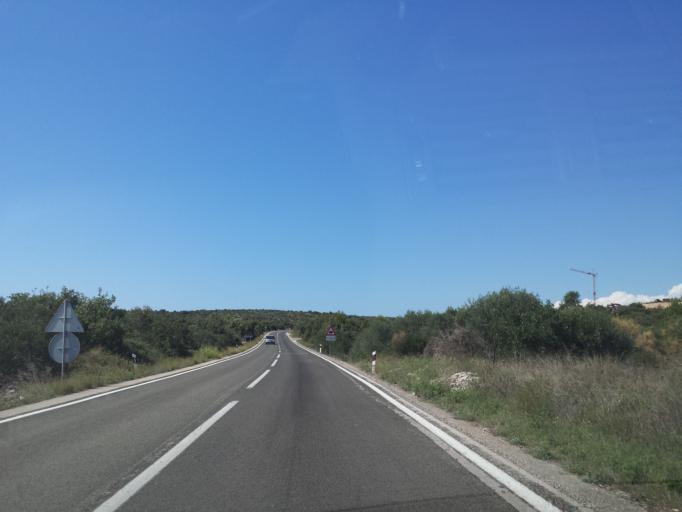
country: HR
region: Sibensko-Kniniska
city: Rogoznica
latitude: 43.5433
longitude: 15.9660
